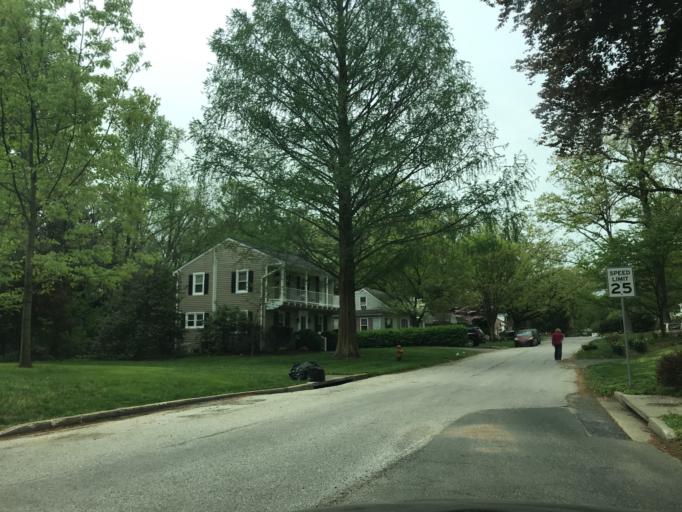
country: US
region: Maryland
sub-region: Baltimore County
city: Catonsville
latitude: 39.2589
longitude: -76.7458
